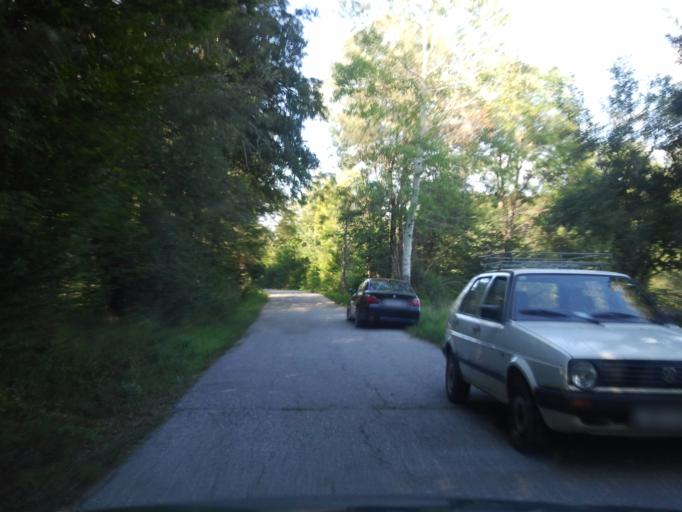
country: HR
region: Zadarska
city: Obrovac
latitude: 44.3347
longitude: 15.6423
